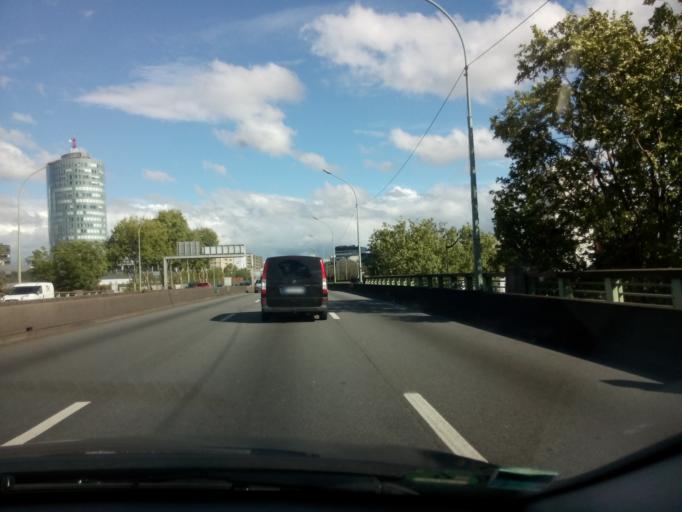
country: FR
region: Ile-de-France
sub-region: Departement des Hauts-de-Seine
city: Issy-les-Moulineaux
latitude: 48.8340
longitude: 2.2766
